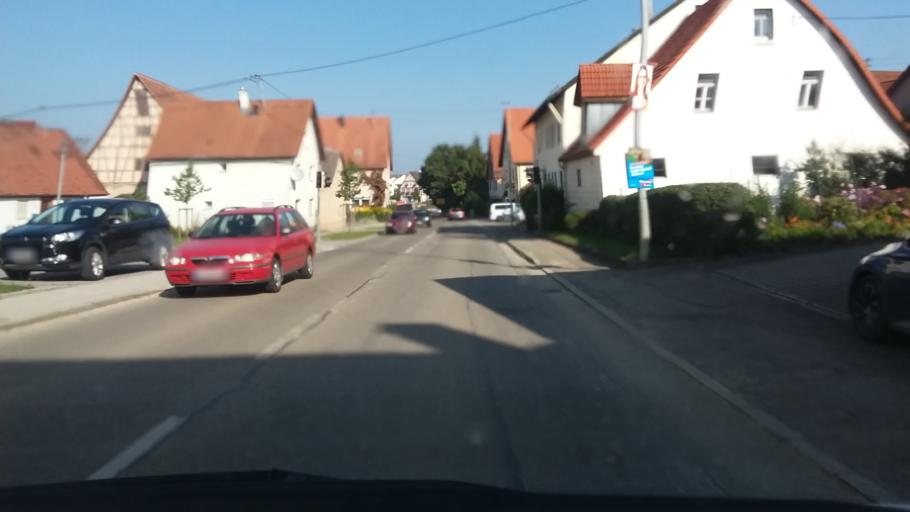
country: DE
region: Baden-Wuerttemberg
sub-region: Tuebingen Region
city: Nellingen
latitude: 48.5402
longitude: 9.7920
